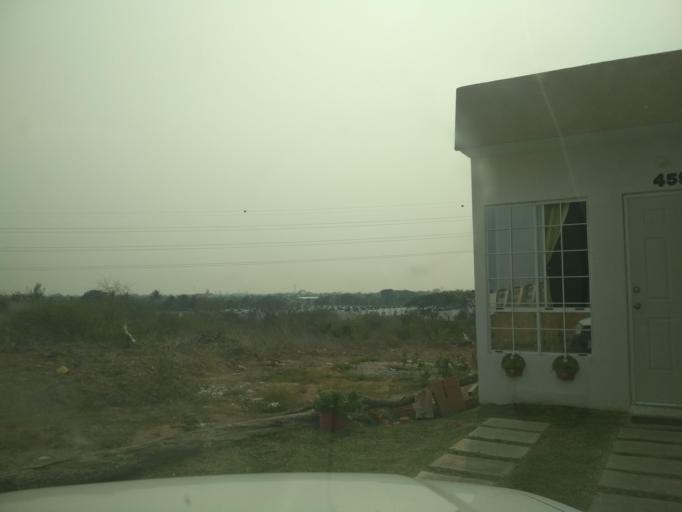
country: MX
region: Veracruz
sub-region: Veracruz
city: Las Amapolas
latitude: 19.1390
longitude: -96.2246
